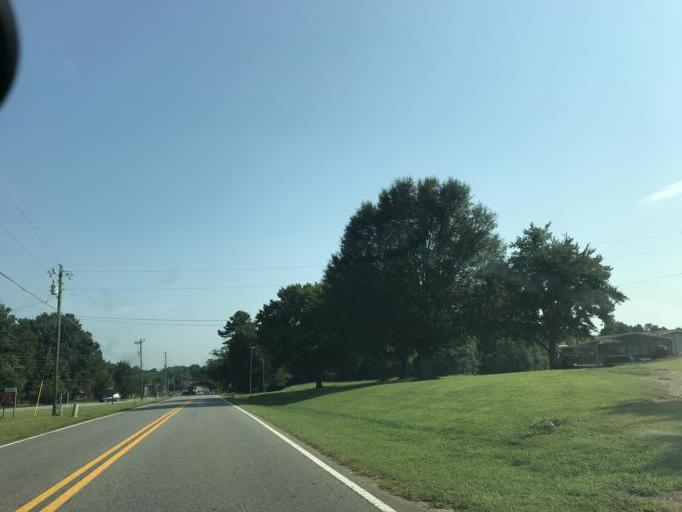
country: US
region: Georgia
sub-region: Forsyth County
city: Cumming
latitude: 34.2428
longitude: -84.1707
